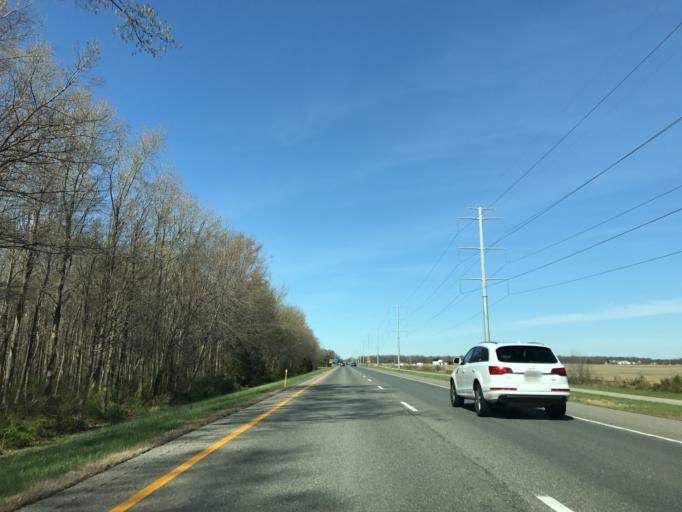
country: US
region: Maryland
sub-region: Queen Anne's County
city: Centreville
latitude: 39.0744
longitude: -75.9818
